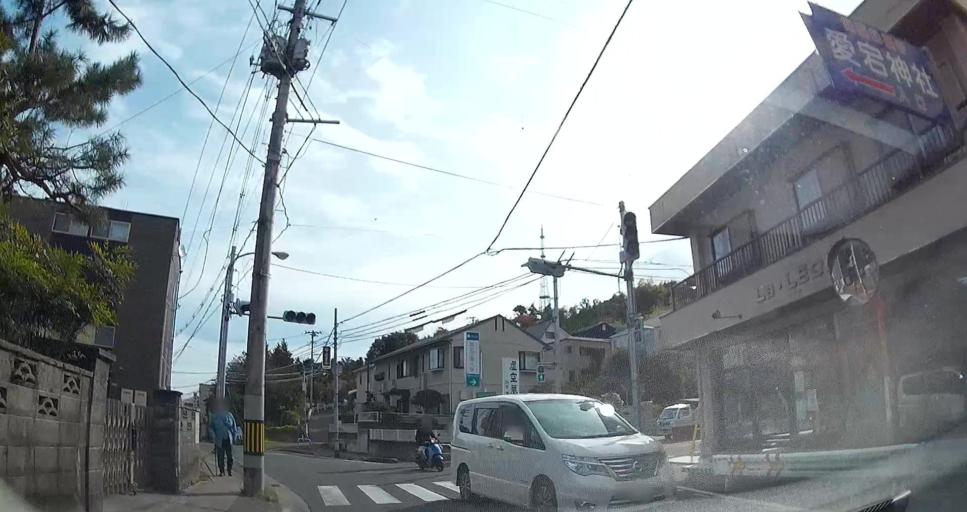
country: JP
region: Miyagi
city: Sendai
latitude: 38.2436
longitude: 140.8736
